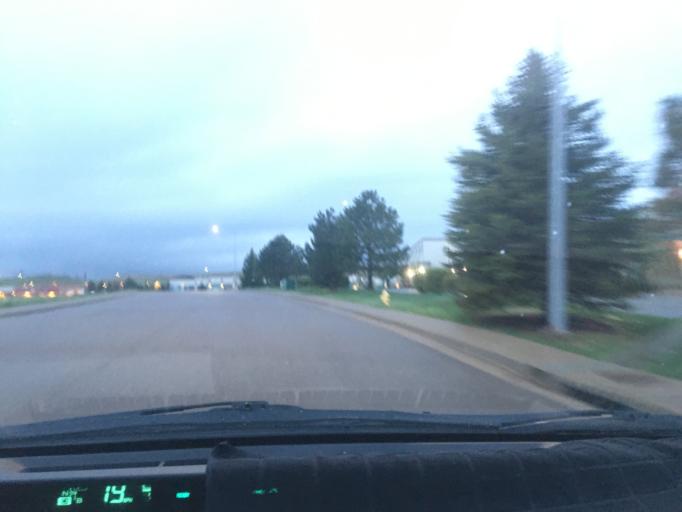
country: US
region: Colorado
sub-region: Broomfield County
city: Broomfield
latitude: 39.9054
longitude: -105.0993
